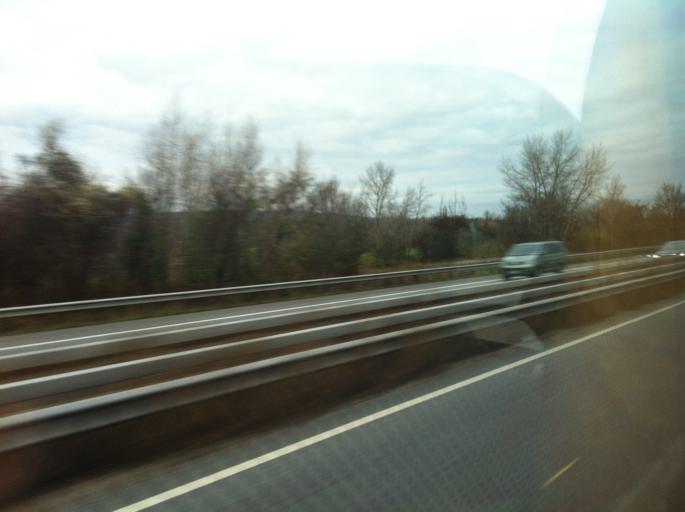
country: DE
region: Hesse
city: Geisenheim
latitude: 49.9753
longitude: 7.9919
